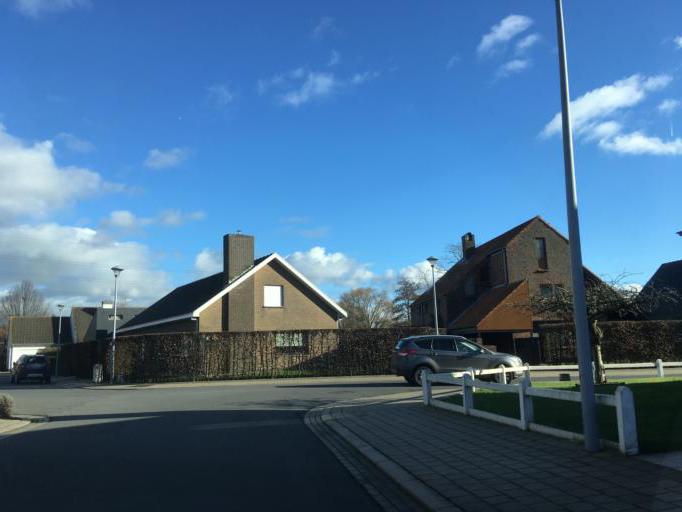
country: BE
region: Flanders
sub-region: Provincie West-Vlaanderen
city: Roeselare
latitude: 50.9490
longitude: 3.1437
